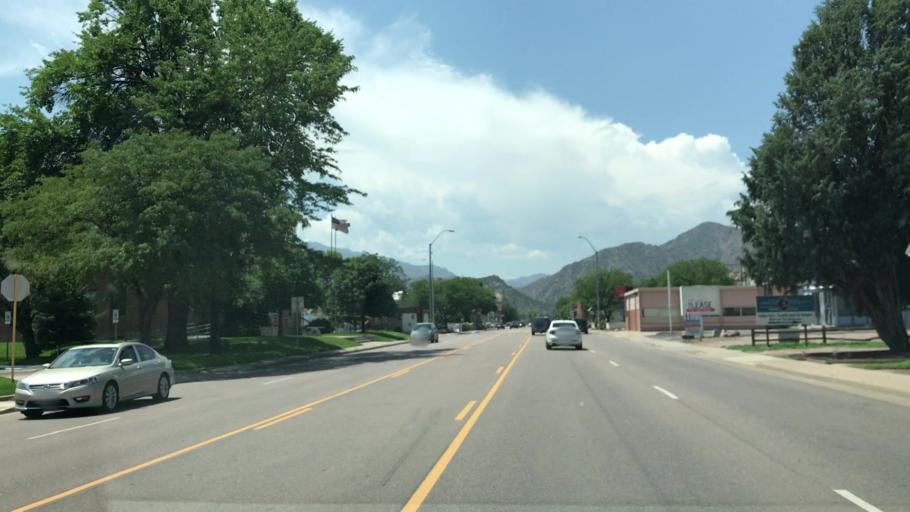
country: US
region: Colorado
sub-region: Fremont County
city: Canon City
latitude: 38.4409
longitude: -105.2377
